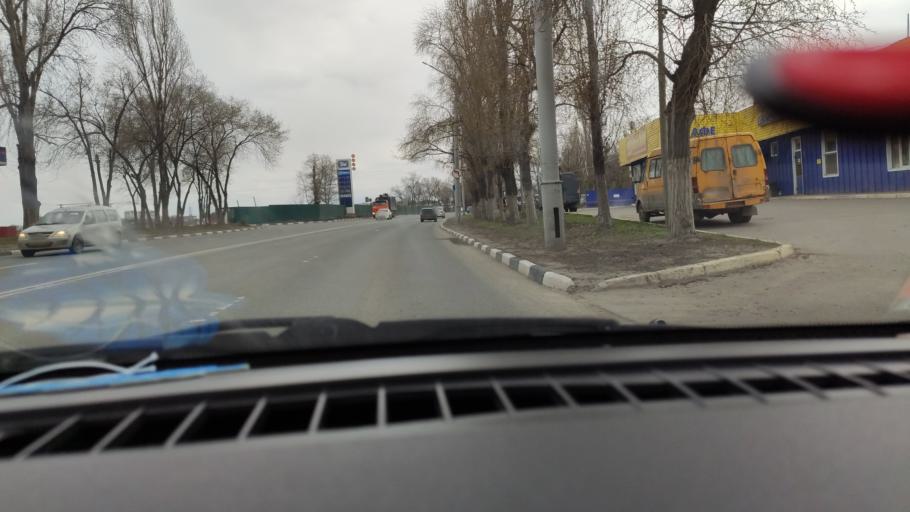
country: RU
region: Saratov
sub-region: Saratovskiy Rayon
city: Saratov
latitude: 51.5766
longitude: 45.9876
